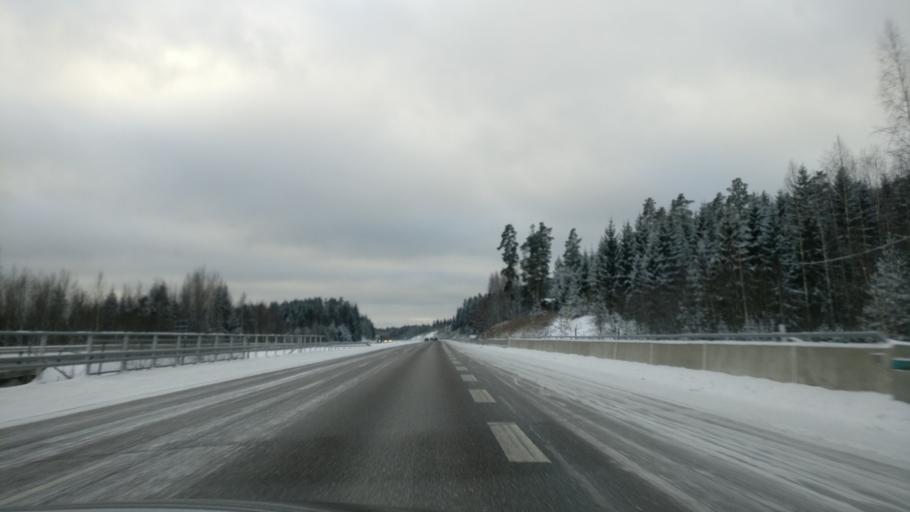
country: FI
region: Paijanne Tavastia
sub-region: Lahti
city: Nastola
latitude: 61.0639
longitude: 25.8695
